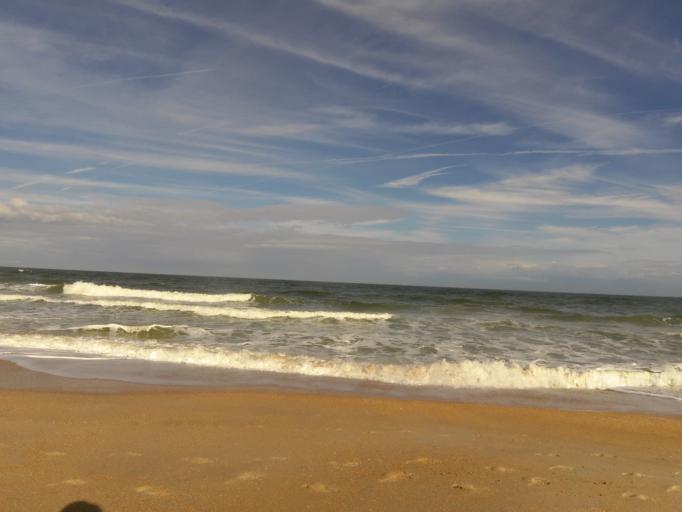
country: US
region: Florida
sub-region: Saint Johns County
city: Villano Beach
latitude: 29.9220
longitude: -81.2923
